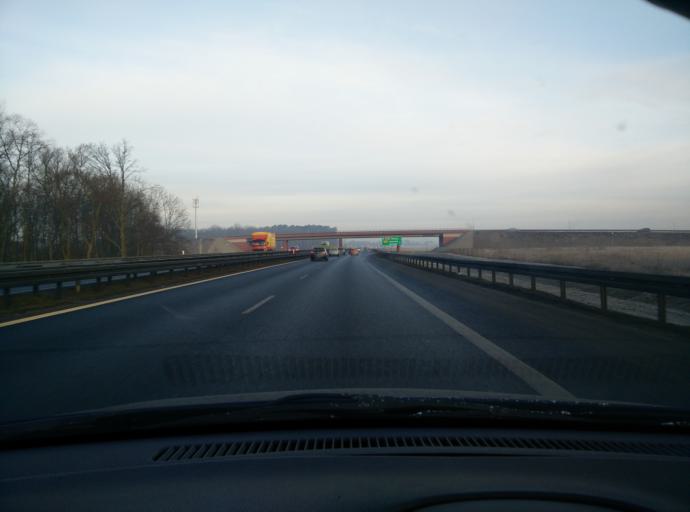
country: PL
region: Greater Poland Voivodeship
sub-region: Powiat poznanski
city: Daszewice
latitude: 52.3215
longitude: 17.0354
